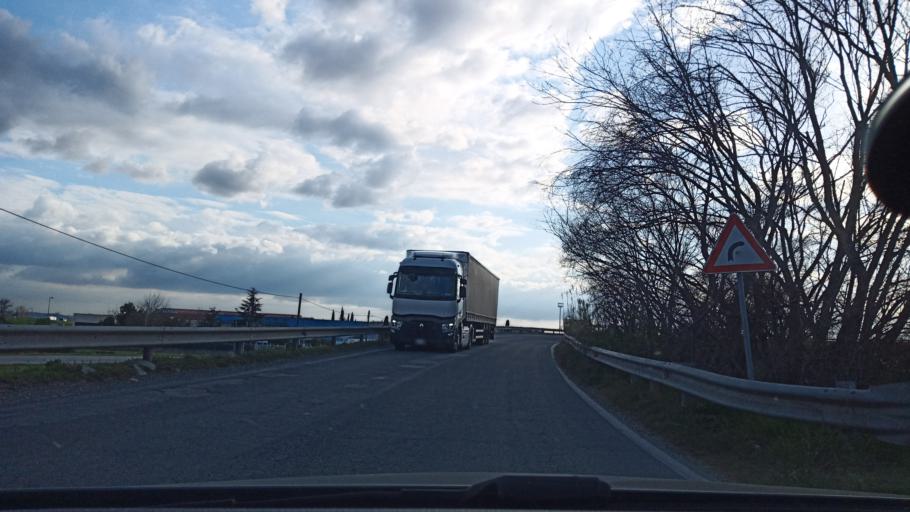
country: IT
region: Latium
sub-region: Citta metropolitana di Roma Capitale
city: Fiano Romano
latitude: 42.1477
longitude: 12.6223
